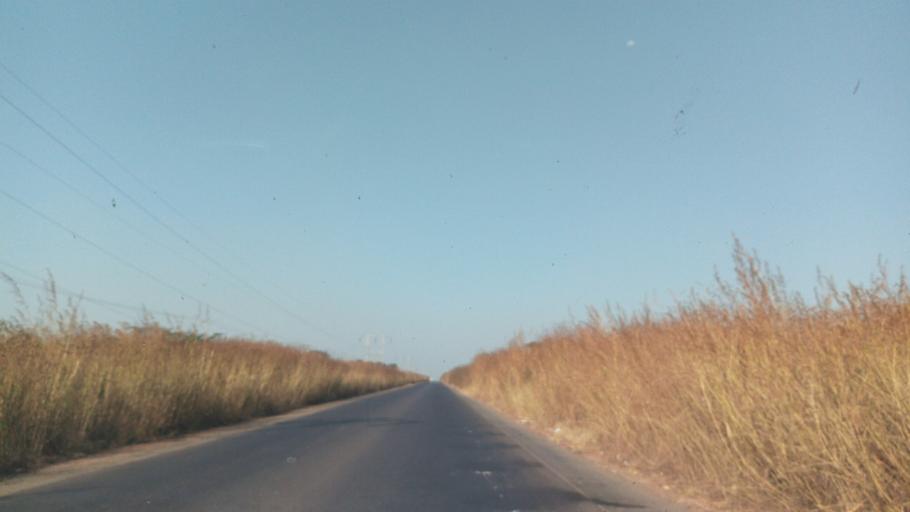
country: CD
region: Katanga
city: Likasi
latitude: -11.0018
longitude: 26.8648
